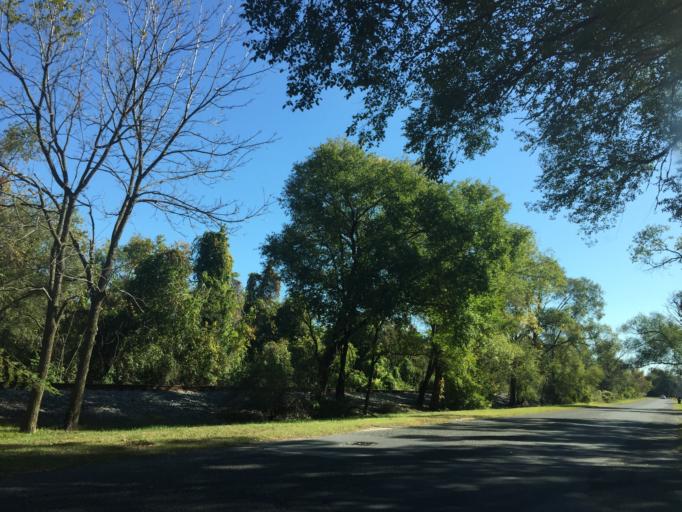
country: US
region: Maryland
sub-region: Baltimore County
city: Dundalk
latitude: 39.2573
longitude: -76.5061
